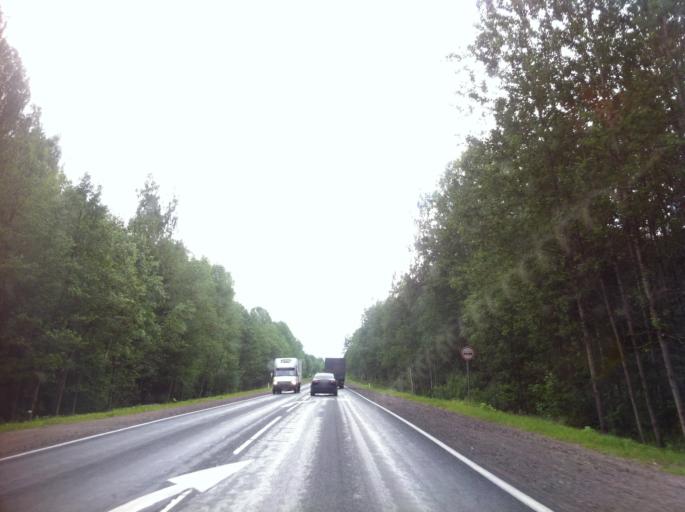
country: RU
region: Pskov
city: Strugi-Krasnyye
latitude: 58.1139
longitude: 29.1141
